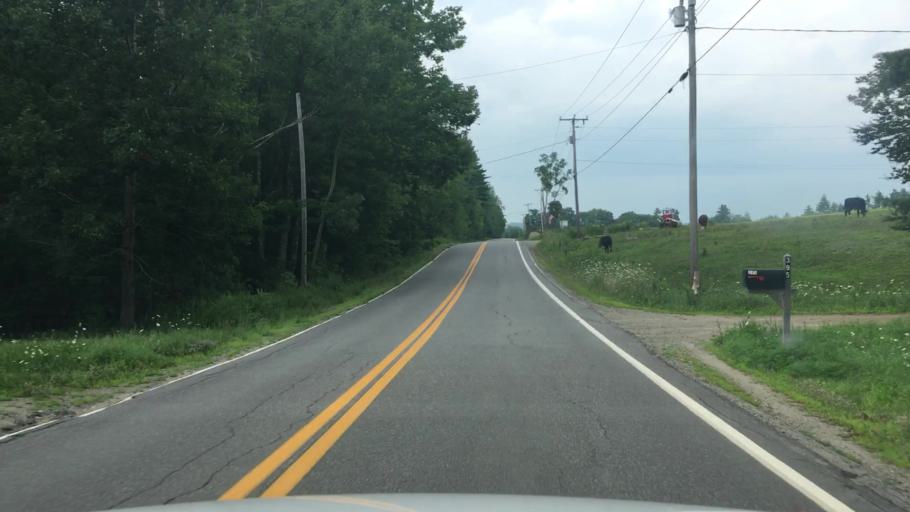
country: US
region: Maine
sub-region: Knox County
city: Washington
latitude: 44.2999
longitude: -69.3617
